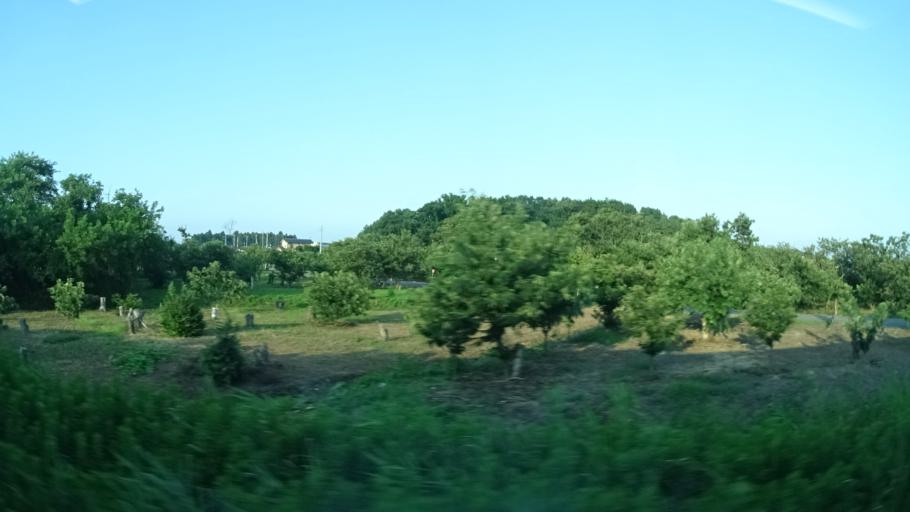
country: JP
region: Ibaraki
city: Tomobe
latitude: 36.2831
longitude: 140.2780
